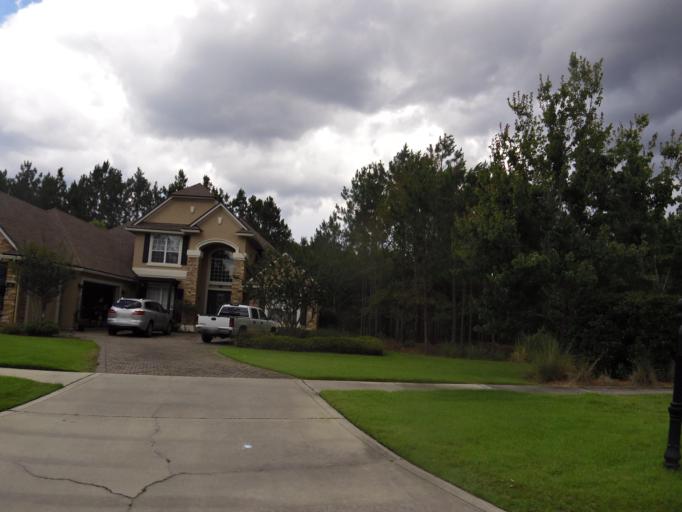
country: US
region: Florida
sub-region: Saint Johns County
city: Fruit Cove
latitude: 30.0636
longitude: -81.6369
